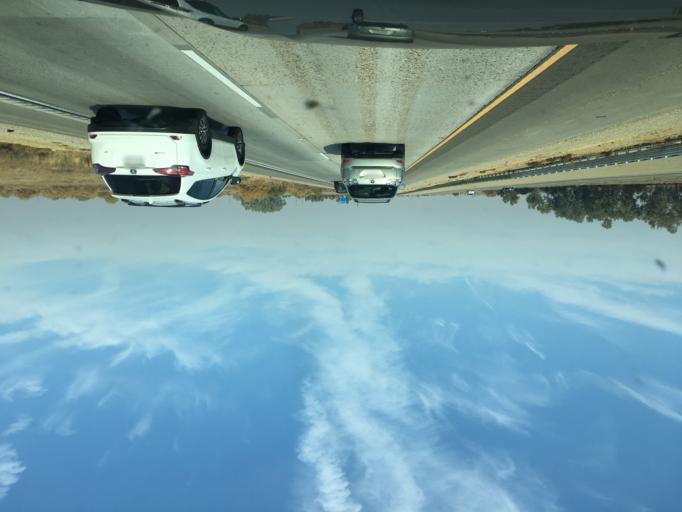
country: US
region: California
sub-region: Kern County
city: Lost Hills
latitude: 35.5956
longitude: -119.6355
